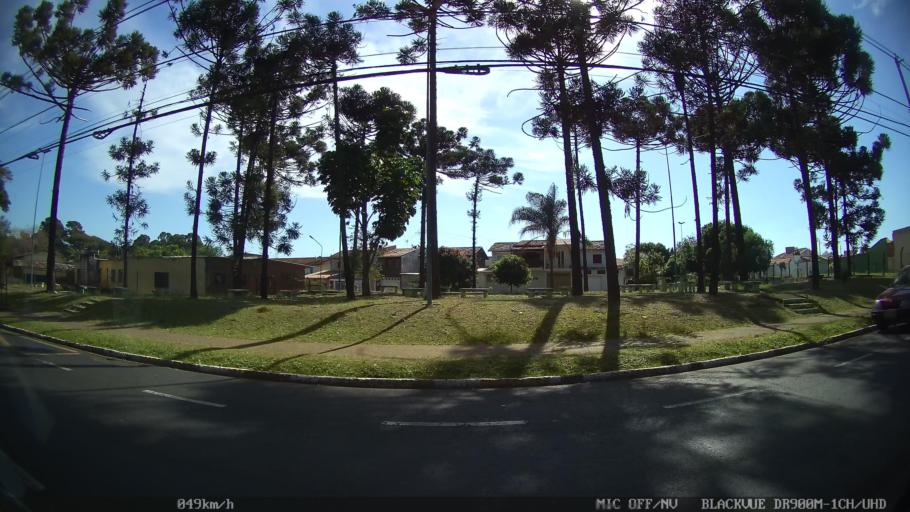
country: BR
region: Sao Paulo
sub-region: Franca
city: Franca
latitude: -20.5115
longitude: -47.4029
